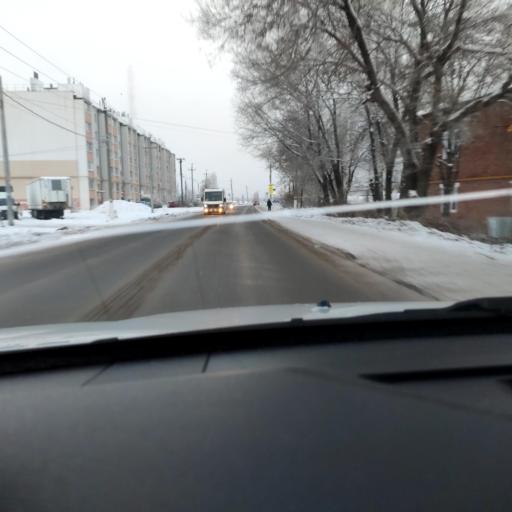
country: RU
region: Samara
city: Smyshlyayevka
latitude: 53.2498
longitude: 50.4814
